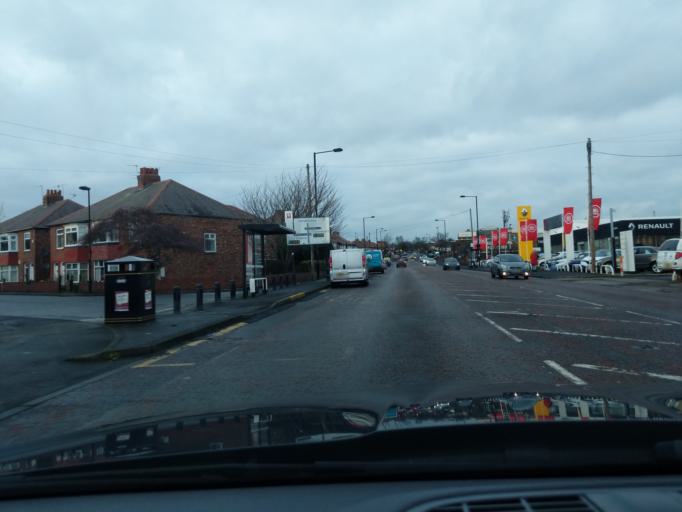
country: GB
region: England
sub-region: Borough of North Tyneside
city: Wallsend
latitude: 54.9930
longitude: -1.5647
